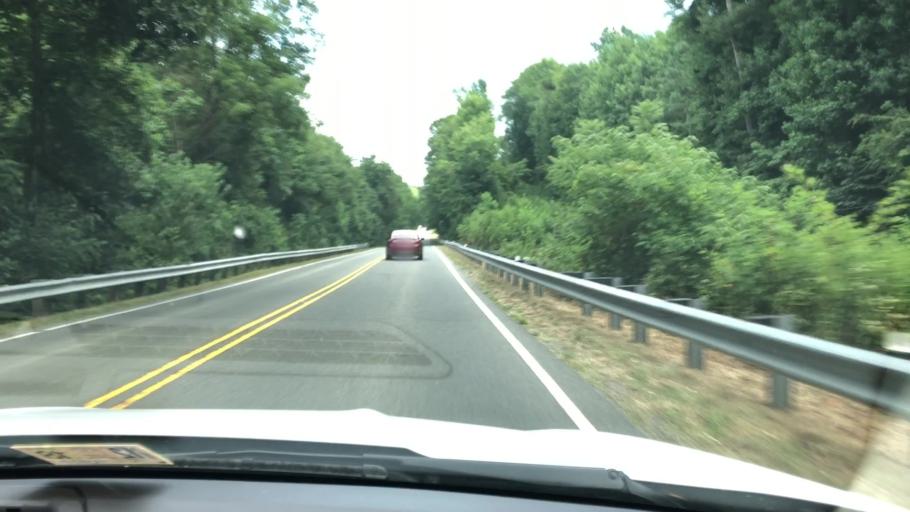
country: US
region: Virginia
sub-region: Lancaster County
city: Lancaster
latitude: 37.7690
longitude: -76.4967
